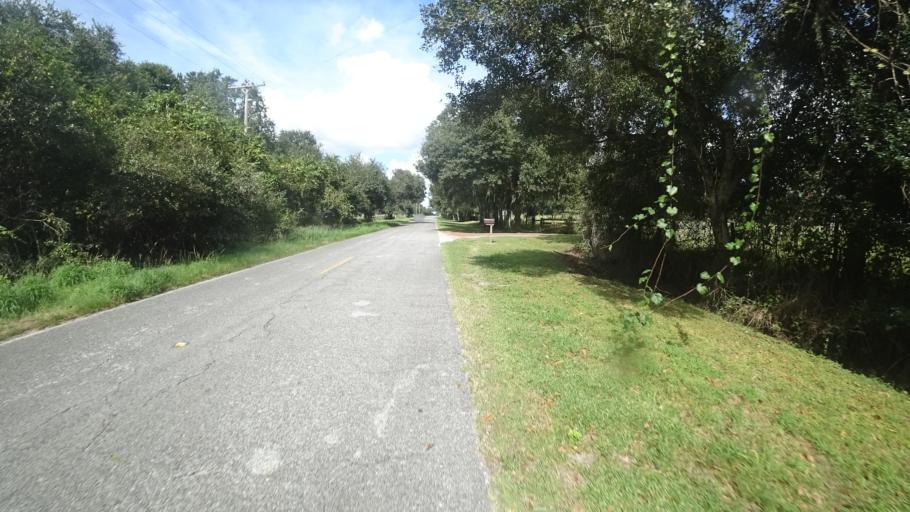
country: US
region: Florida
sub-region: Hillsborough County
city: Wimauma
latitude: 27.6473
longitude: -82.2286
